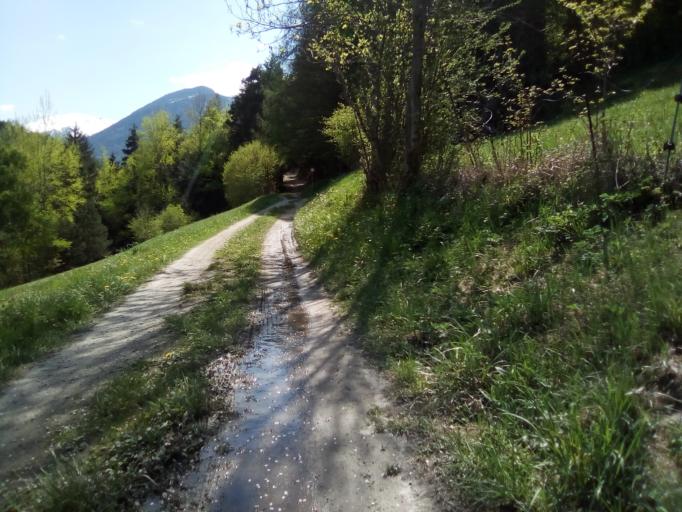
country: CH
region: Valais
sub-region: Entremont District
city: Orsieres
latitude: 46.0495
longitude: 7.1466
